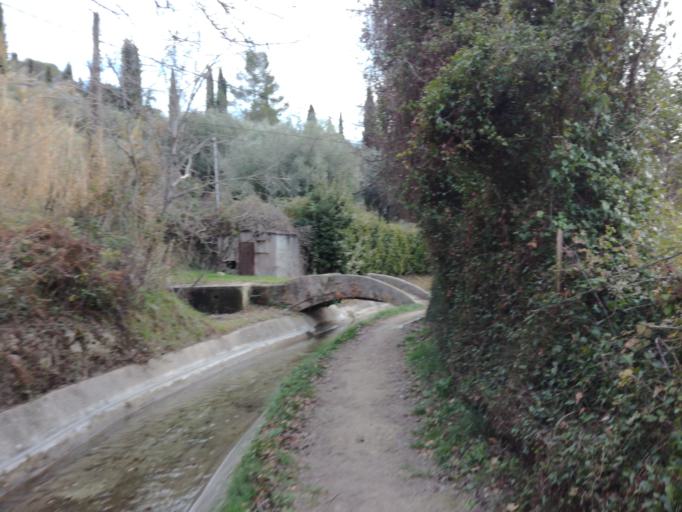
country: FR
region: Provence-Alpes-Cote d'Azur
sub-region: Departement des Alpes-Maritimes
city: Mouans-Sartoux
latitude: 43.6182
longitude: 6.9824
